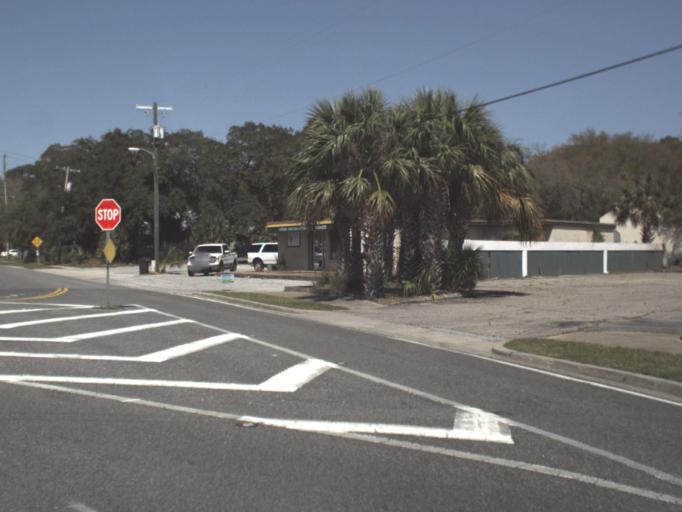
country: US
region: Florida
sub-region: Okaloosa County
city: Fort Walton Beach
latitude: 30.4076
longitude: -86.6029
